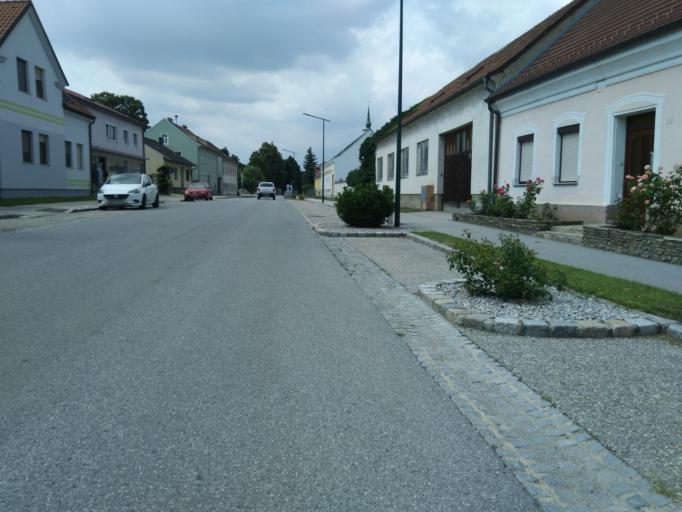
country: AT
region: Lower Austria
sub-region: Politischer Bezirk Ganserndorf
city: Ganserndorf
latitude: 48.3650
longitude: 16.7007
